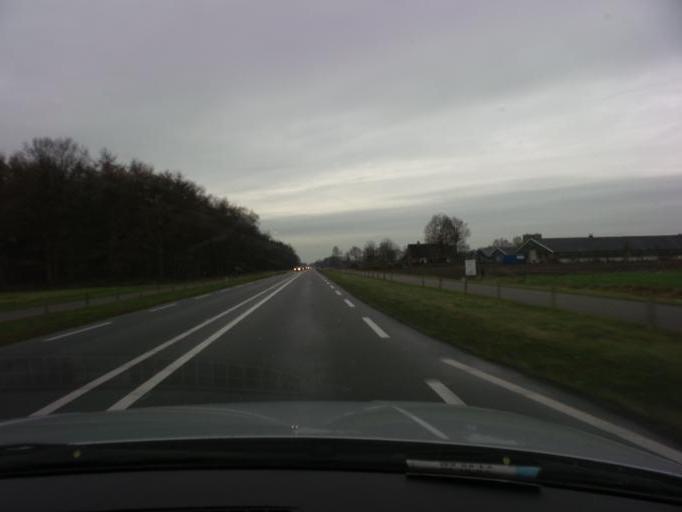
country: NL
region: Overijssel
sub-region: Gemeente Dalfsen
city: Dalfsen
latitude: 52.5292
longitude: 6.2747
